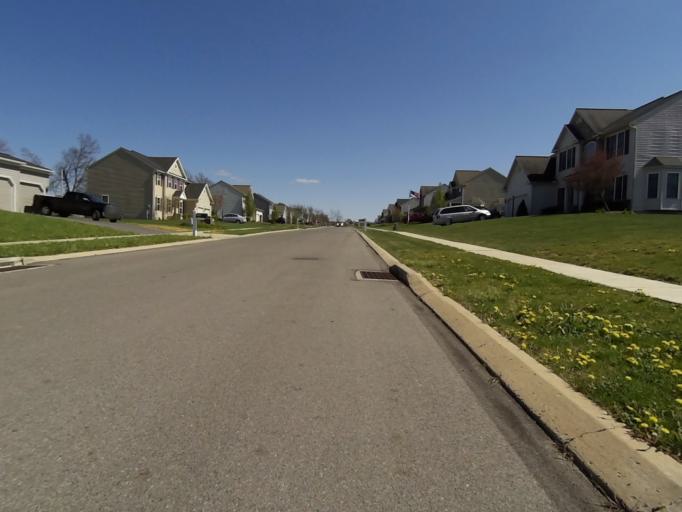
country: US
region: Pennsylvania
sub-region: Centre County
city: Houserville
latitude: 40.8831
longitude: -77.8335
